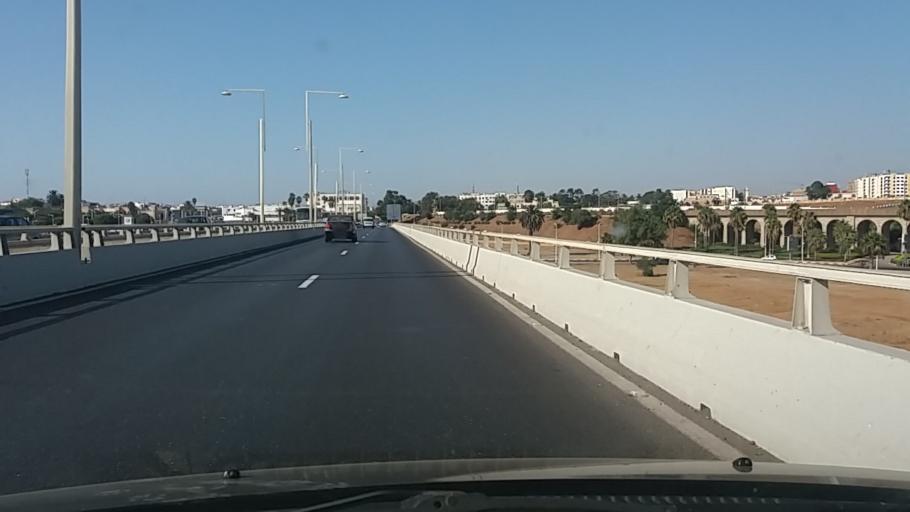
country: MA
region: Rabat-Sale-Zemmour-Zaer
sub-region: Rabat
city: Rabat
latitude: 34.0316
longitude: -6.8182
